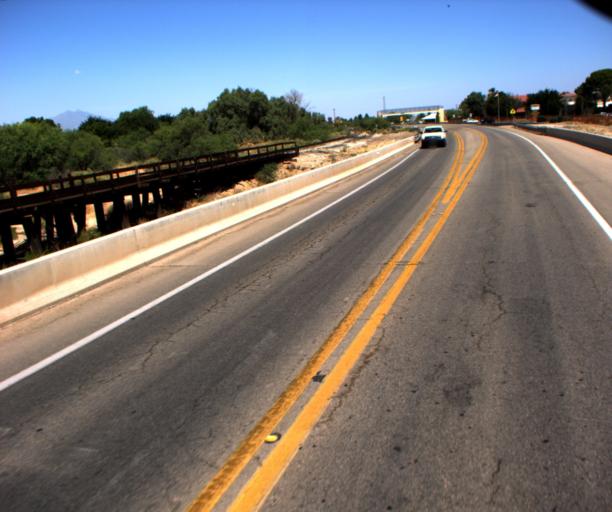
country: US
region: Arizona
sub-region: Graham County
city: Bylas
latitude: 33.0346
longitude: -109.9605
